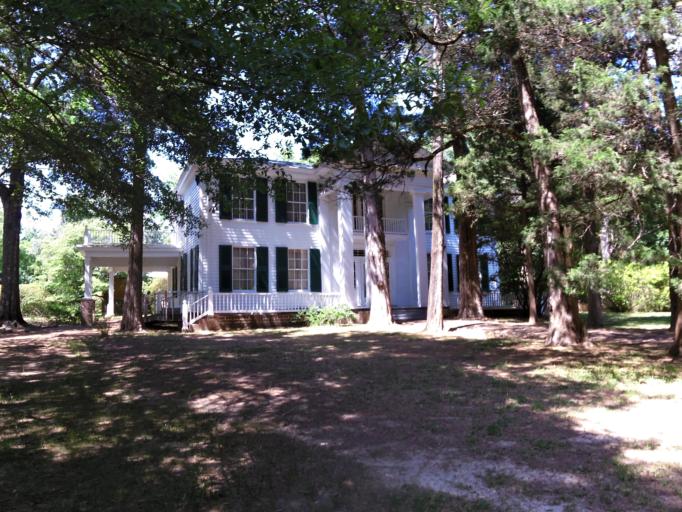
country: US
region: Mississippi
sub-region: Lafayette County
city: University
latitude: 34.3596
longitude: -89.5249
